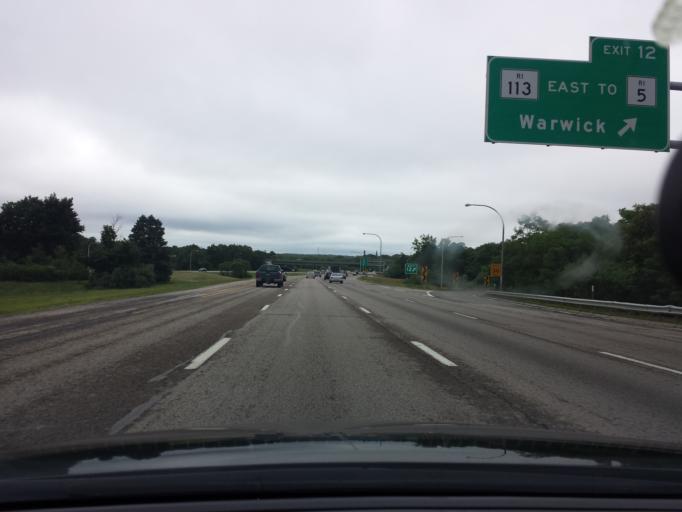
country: US
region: Rhode Island
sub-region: Kent County
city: West Warwick
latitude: 41.7125
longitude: -71.4713
